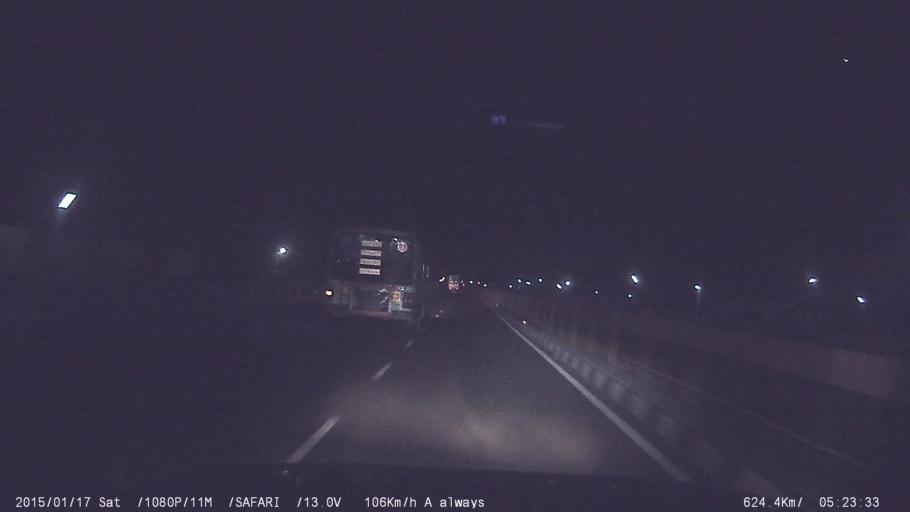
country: IN
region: Tamil Nadu
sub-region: Vellore
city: Katpadi
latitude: 12.9469
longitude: 79.2060
